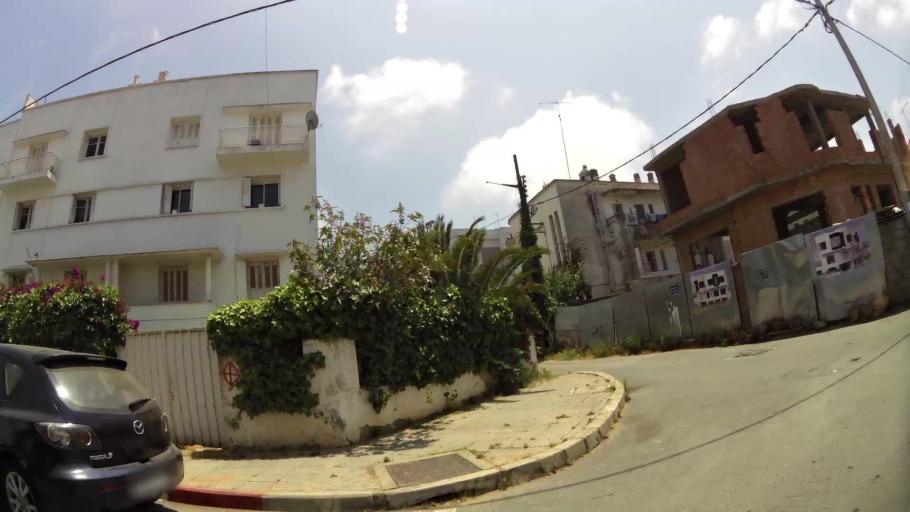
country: MA
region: Rabat-Sale-Zemmour-Zaer
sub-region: Rabat
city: Rabat
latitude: 34.0104
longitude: -6.8437
